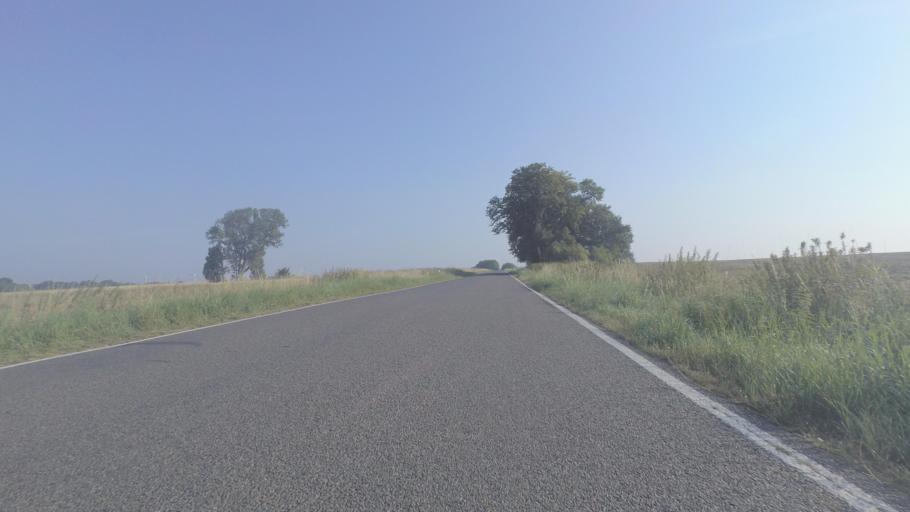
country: DE
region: Brandenburg
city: Heiligengrabe
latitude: 53.2737
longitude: 12.3414
